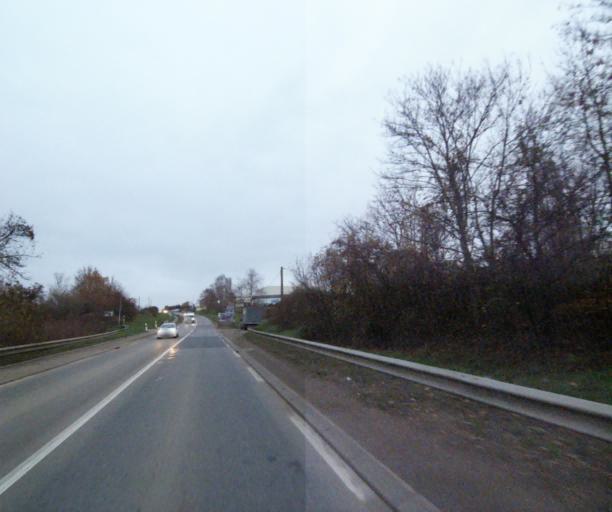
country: FR
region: Ile-de-France
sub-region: Departement des Yvelines
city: Orgeval
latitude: 48.9331
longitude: 1.9743
